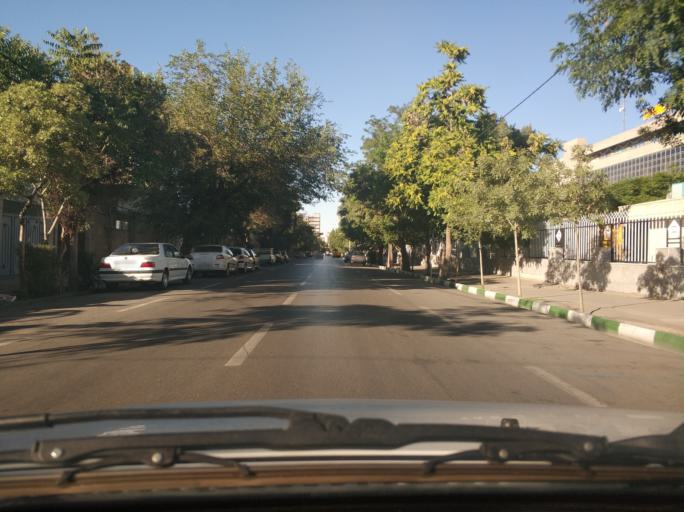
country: IR
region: Razavi Khorasan
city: Mashhad
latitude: 36.2778
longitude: 59.5943
